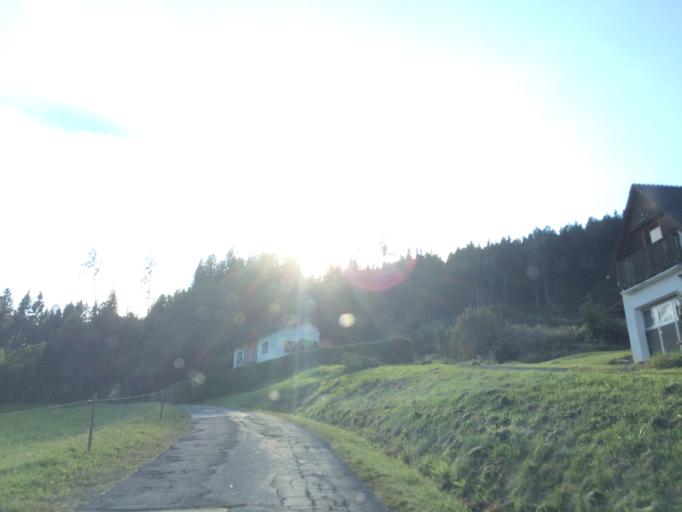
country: AT
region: Styria
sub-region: Politischer Bezirk Leoben
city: Kraubath an der Mur
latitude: 47.3060
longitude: 14.9261
